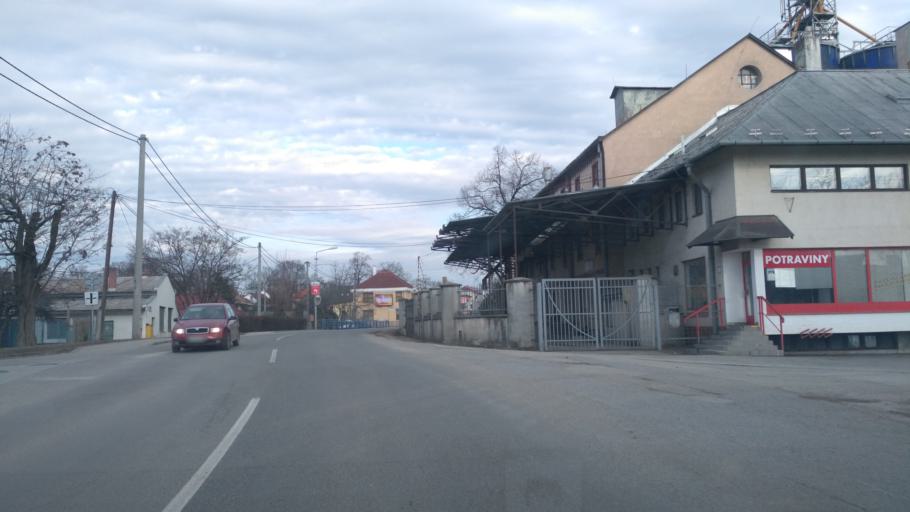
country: SK
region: Kosicky
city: Moldava nad Bodvou
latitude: 48.6099
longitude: 20.9974
